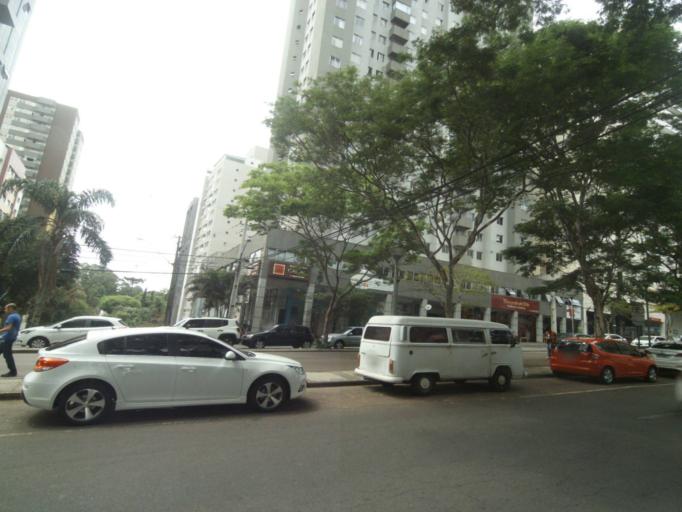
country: BR
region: Parana
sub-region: Curitiba
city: Curitiba
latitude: -25.4338
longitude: -49.3010
